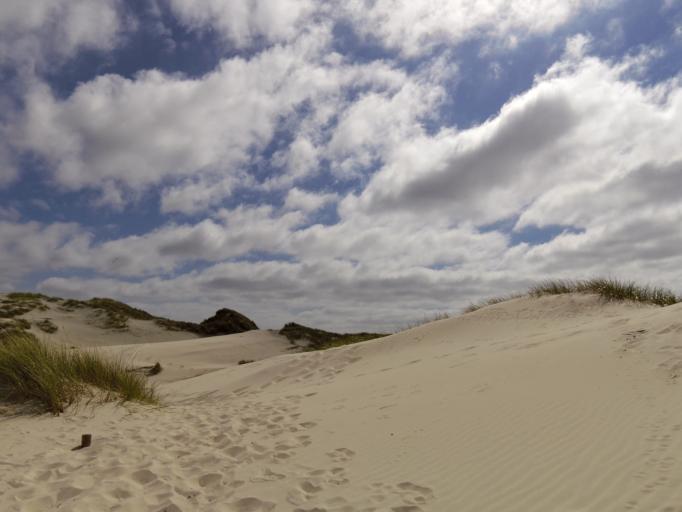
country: DE
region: Schleswig-Holstein
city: Nebel
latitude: 54.6245
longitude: 8.3573
